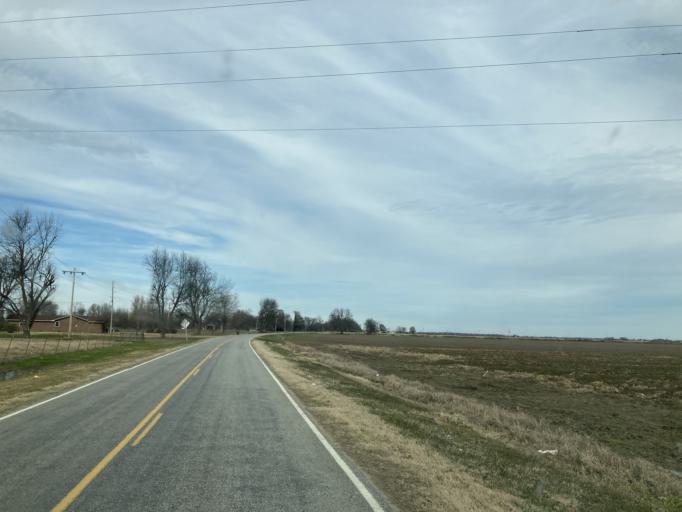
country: US
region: Mississippi
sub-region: Washington County
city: Hollandale
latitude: 33.1852
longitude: -90.6823
